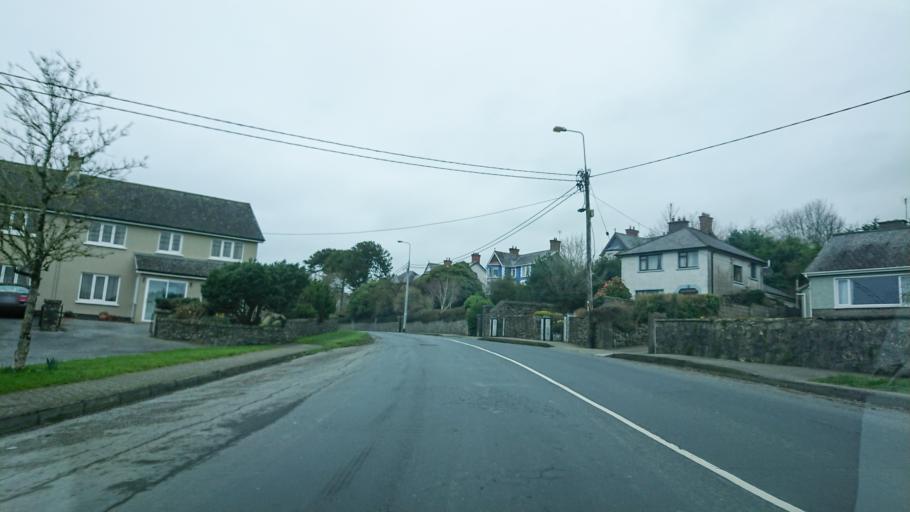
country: IE
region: Munster
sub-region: County Cork
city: Bandon
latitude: 51.7477
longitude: -8.7407
